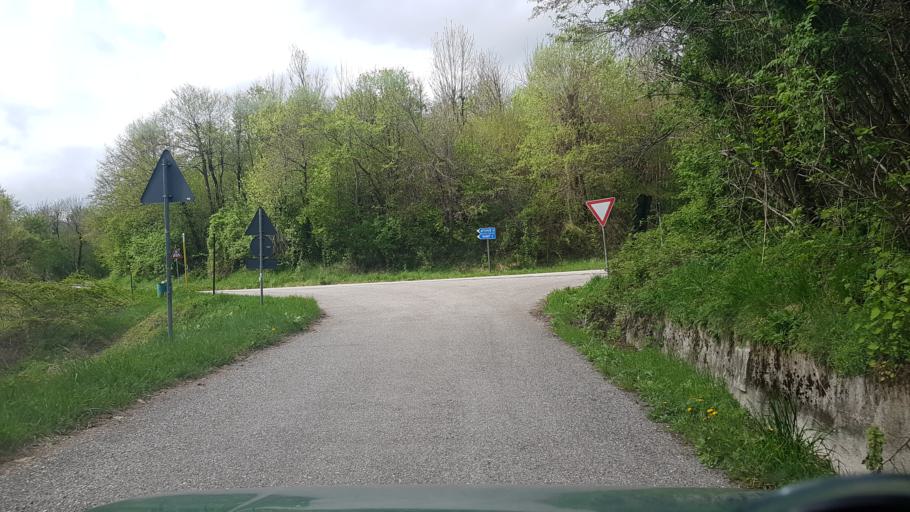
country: IT
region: Friuli Venezia Giulia
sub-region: Provincia di Udine
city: Taipana
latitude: 46.2028
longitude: 13.3595
